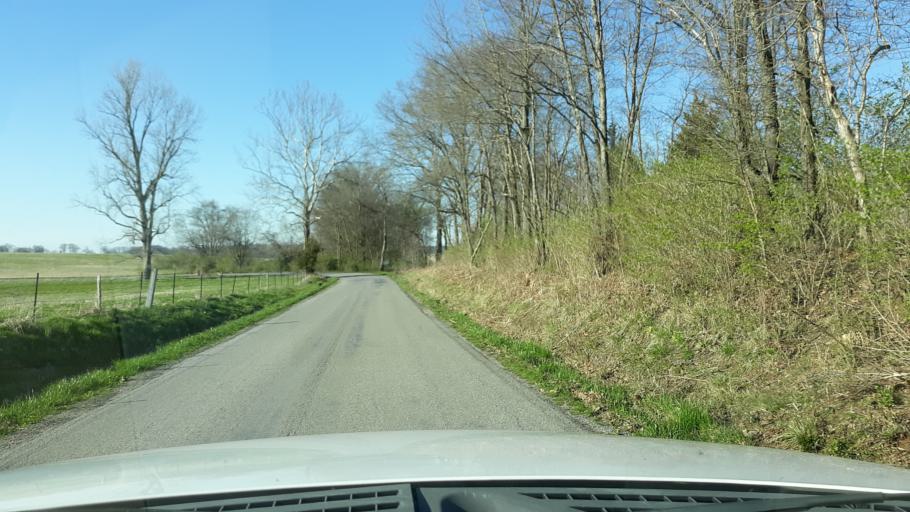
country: US
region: Illinois
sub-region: Saline County
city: Harrisburg
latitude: 37.7633
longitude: -88.5818
